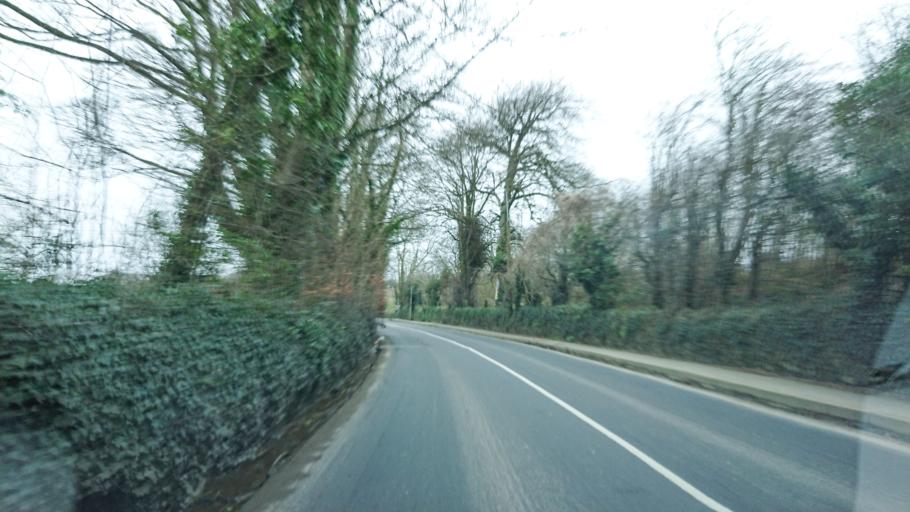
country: IE
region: Munster
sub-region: County Cork
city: Bandon
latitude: 51.7478
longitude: -8.7468
